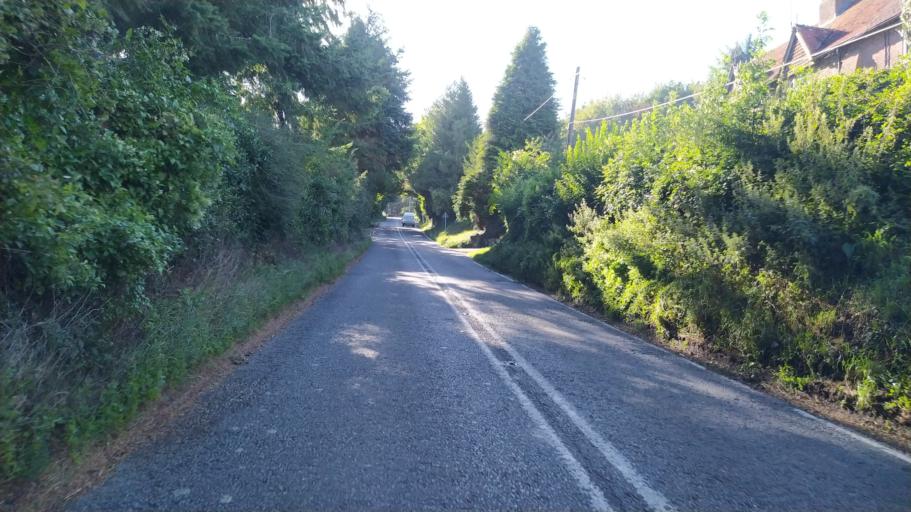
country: GB
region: England
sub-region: Hampshire
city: Kingsley
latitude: 51.1367
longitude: -0.9242
